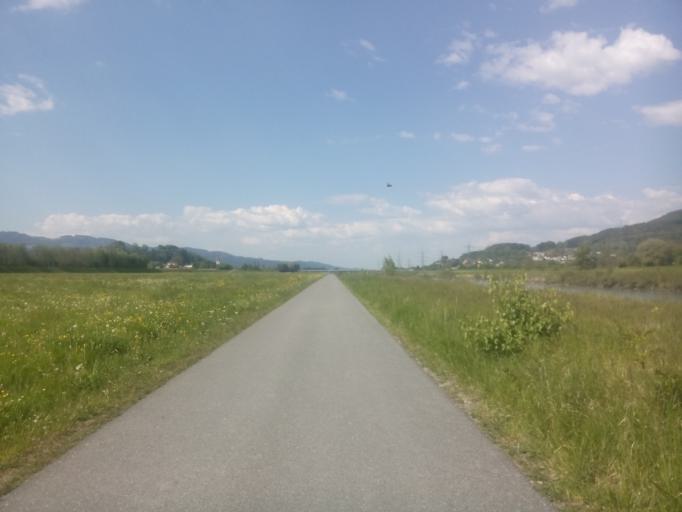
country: AT
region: Vorarlberg
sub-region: Politischer Bezirk Feldkirch
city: Koblach
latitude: 47.3225
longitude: 9.5898
